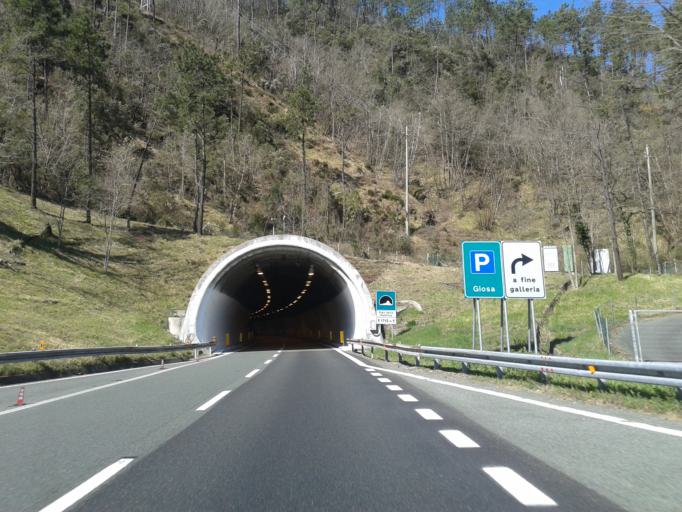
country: IT
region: Liguria
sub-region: Provincia di La Spezia
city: Framura
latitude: 44.2395
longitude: 9.5935
